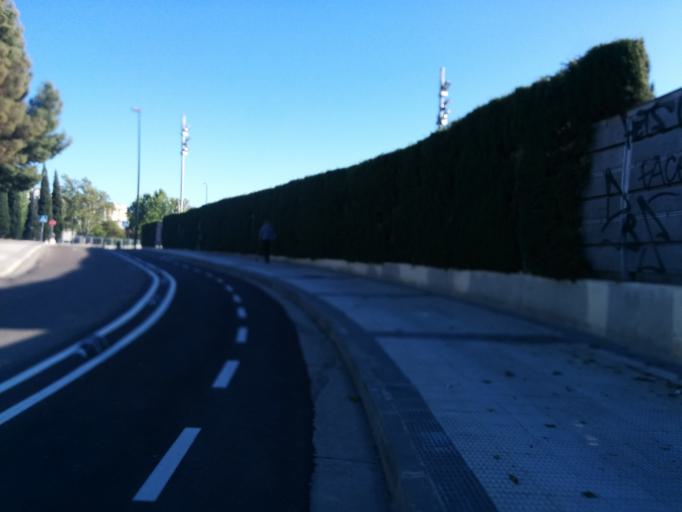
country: ES
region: Aragon
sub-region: Provincia de Zaragoza
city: Zaragoza
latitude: 41.6511
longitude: -0.8645
